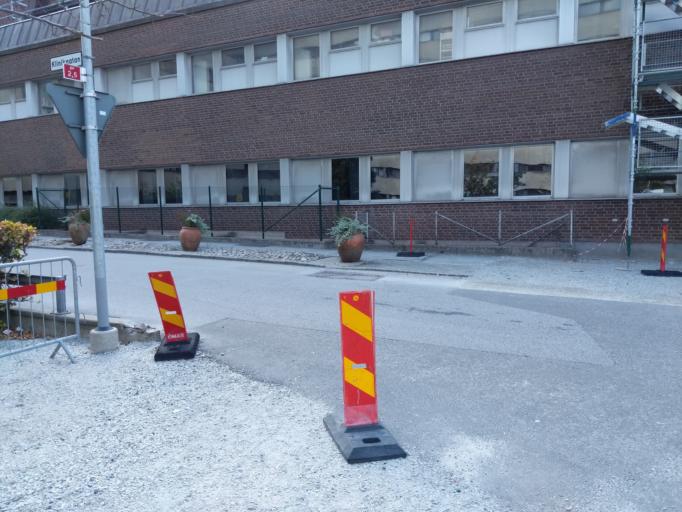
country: SE
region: Skane
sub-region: Lunds Kommun
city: Lund
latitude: 55.7112
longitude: 13.1973
